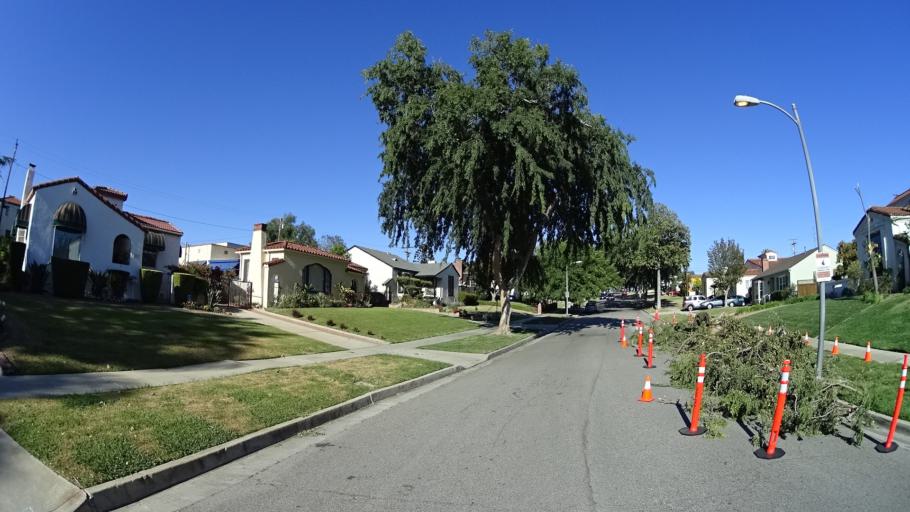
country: US
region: California
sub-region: Los Angeles County
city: Belvedere
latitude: 34.0705
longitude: -118.1588
